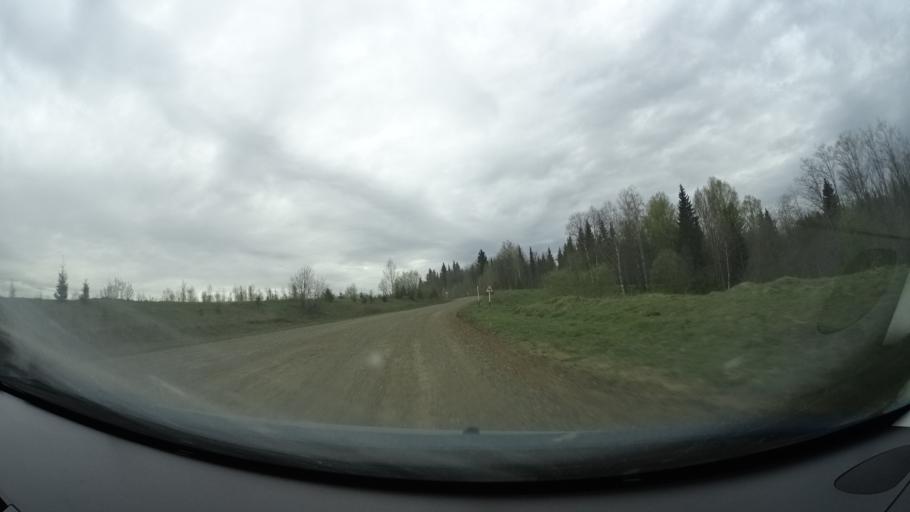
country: RU
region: Perm
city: Kuyeda
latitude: 56.6083
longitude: 55.7133
